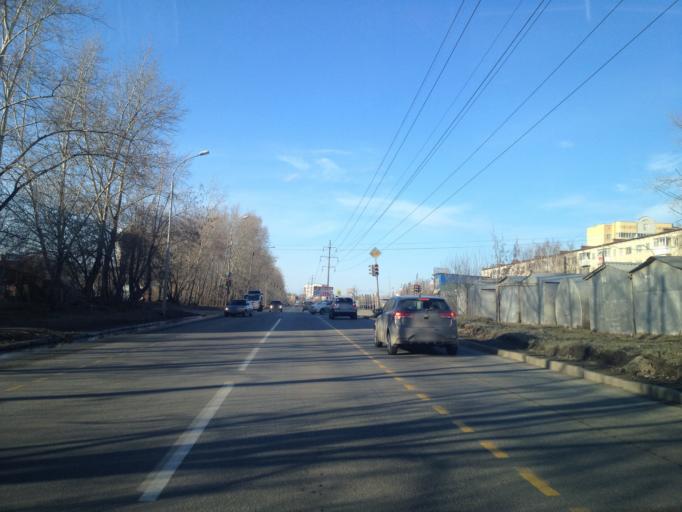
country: RU
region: Sverdlovsk
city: Sovkhoznyy
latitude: 56.7687
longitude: 60.5949
